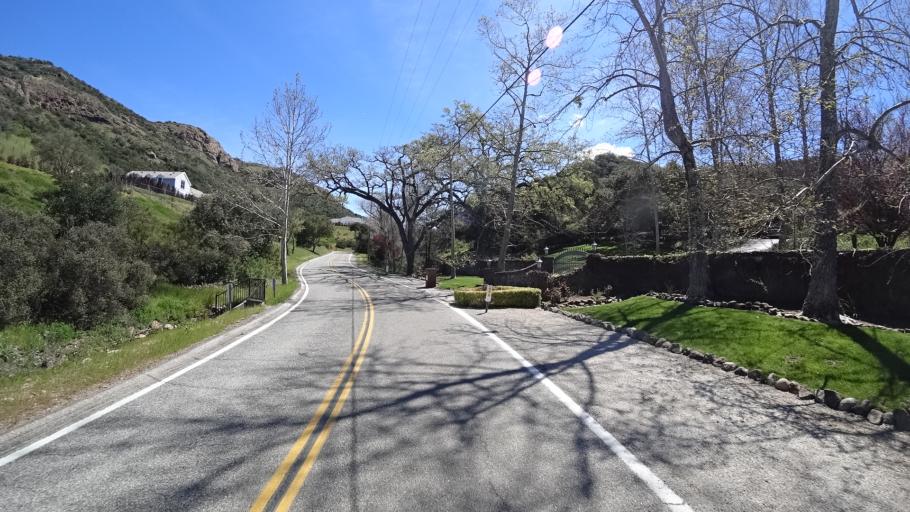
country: US
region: California
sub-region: Ventura County
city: Thousand Oaks
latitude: 34.1253
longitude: -118.8667
